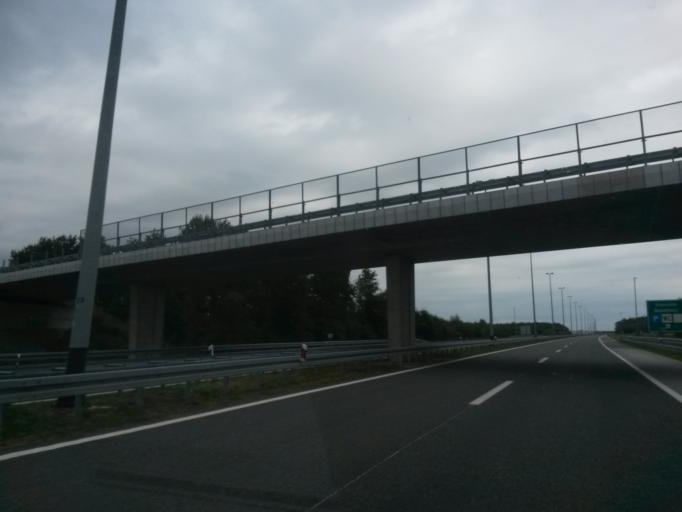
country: HR
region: Osjecko-Baranjska
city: Vuka
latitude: 45.4719
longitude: 18.4819
